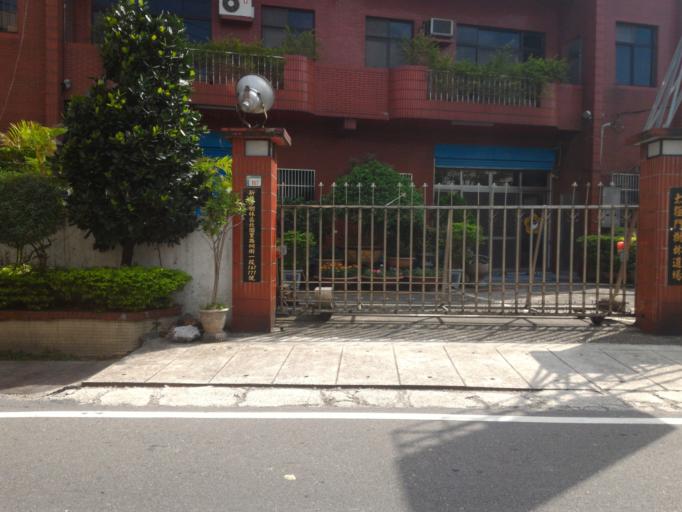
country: TW
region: Taiwan
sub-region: Taoyuan
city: Taoyuan
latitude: 24.9625
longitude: 121.3950
